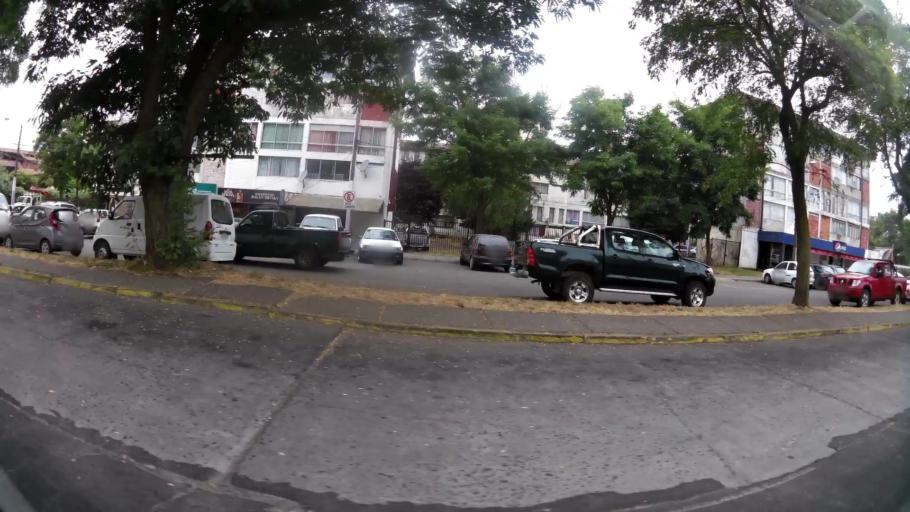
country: CL
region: Biobio
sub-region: Provincia de Concepcion
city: Concepcion
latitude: -36.8178
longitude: -73.0479
